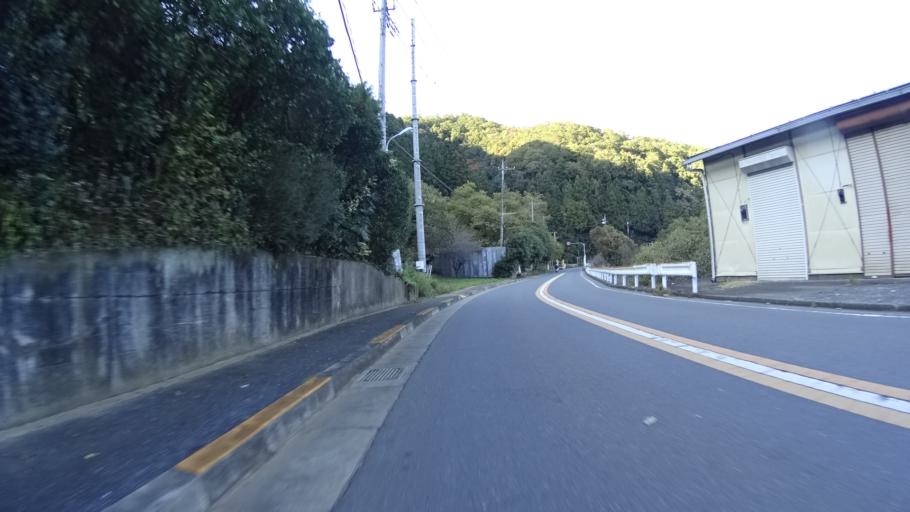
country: JP
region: Tokyo
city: Itsukaichi
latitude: 35.6718
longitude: 139.2163
